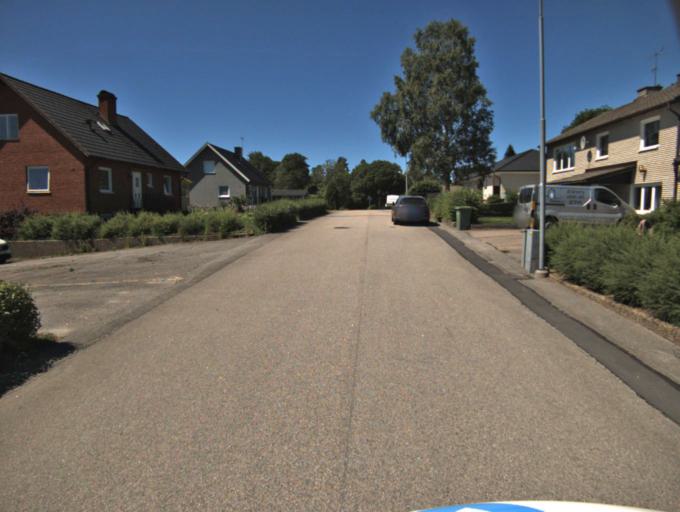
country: SE
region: Vaestra Goetaland
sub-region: Ulricehamns Kommun
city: Ulricehamn
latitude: 57.6671
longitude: 13.4233
